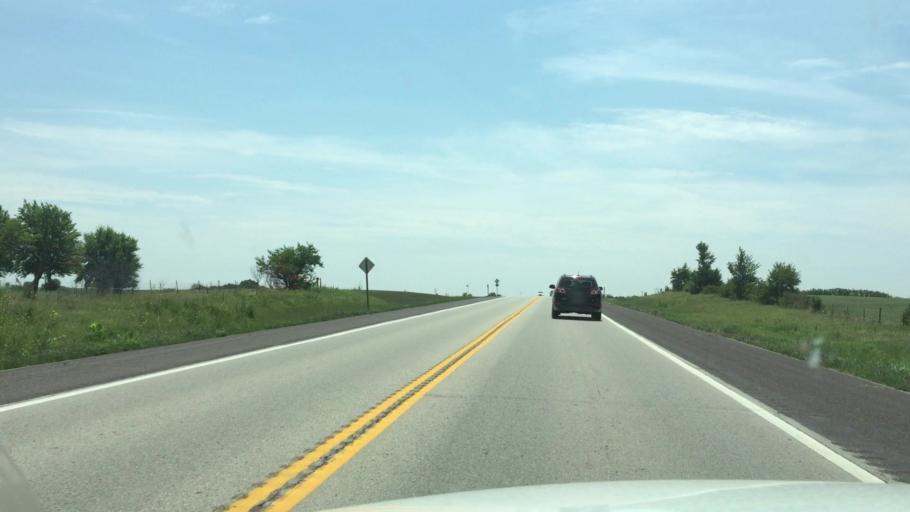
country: US
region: Kansas
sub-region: Jackson County
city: Holton
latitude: 39.5231
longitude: -95.7482
